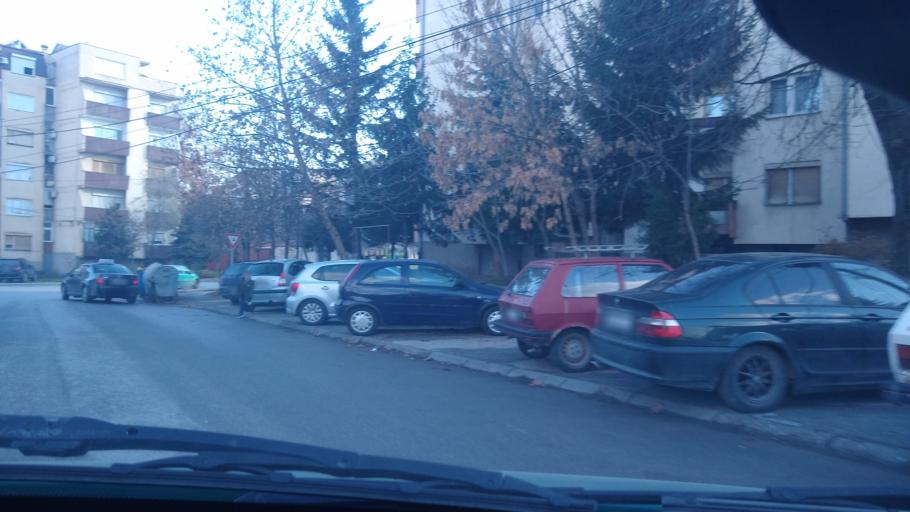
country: MK
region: Bitola
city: Bitola
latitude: 41.0245
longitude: 21.3240
